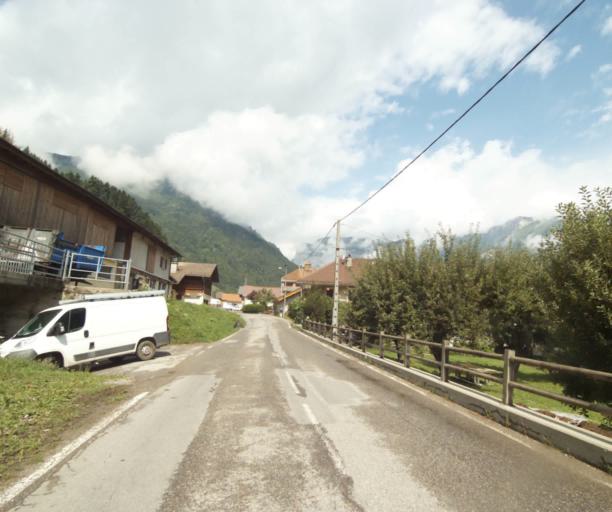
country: FR
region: Rhone-Alpes
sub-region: Departement de la Haute-Savoie
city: Thones
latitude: 45.8842
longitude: 6.3125
